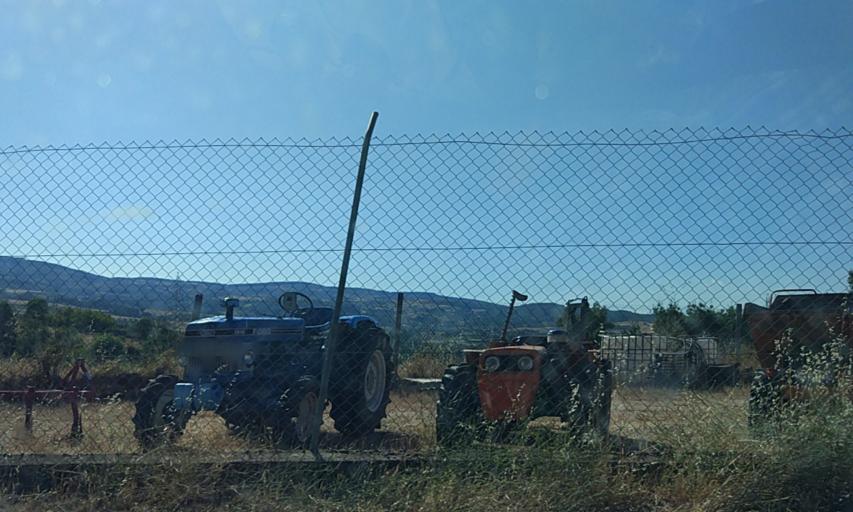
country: PT
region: Braganca
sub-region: Braganca Municipality
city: Braganca
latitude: 41.7775
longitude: -6.7843
